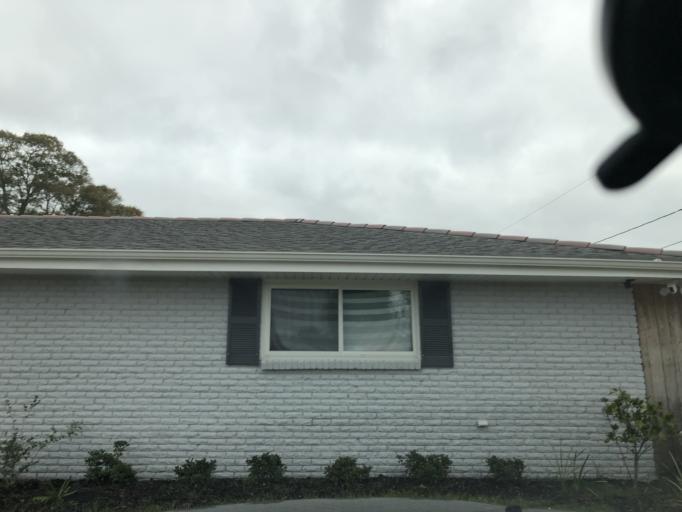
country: US
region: Louisiana
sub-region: Jefferson Parish
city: Metairie Terrace
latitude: 29.9864
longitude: -90.1673
